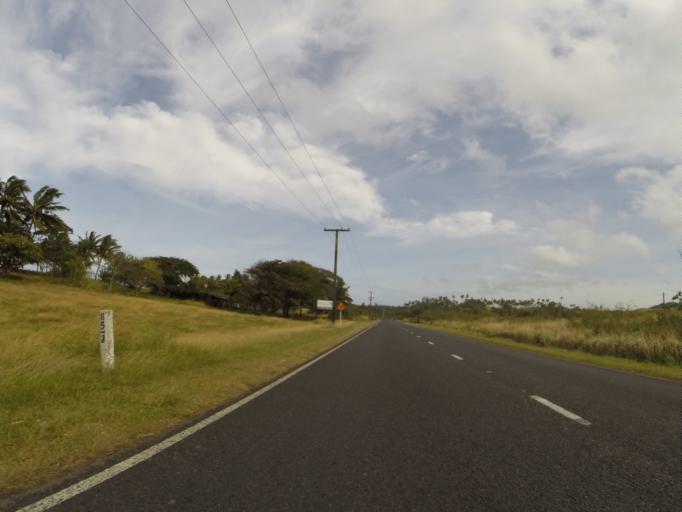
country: FJ
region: Western
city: Nadi
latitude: -18.1659
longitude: 177.4737
